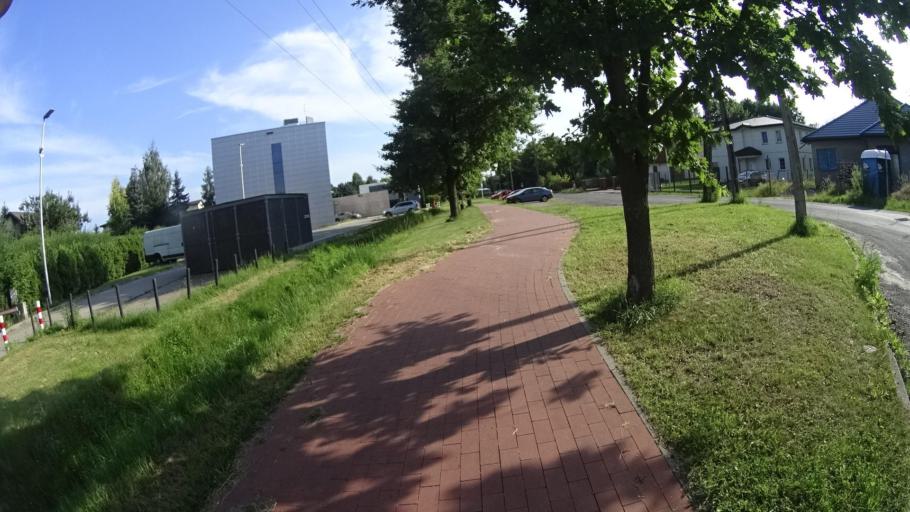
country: PL
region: Masovian Voivodeship
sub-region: Powiat pruszkowski
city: Nadarzyn
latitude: 52.0979
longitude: 20.8023
